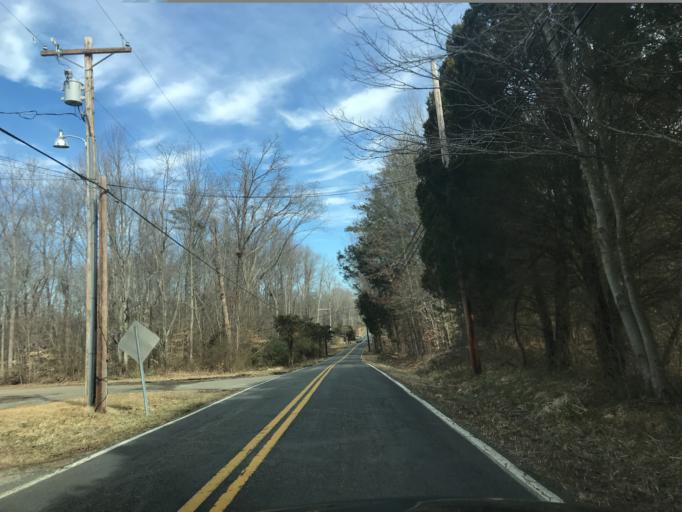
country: US
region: Maryland
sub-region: Charles County
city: La Plata
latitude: 38.5057
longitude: -76.9835
